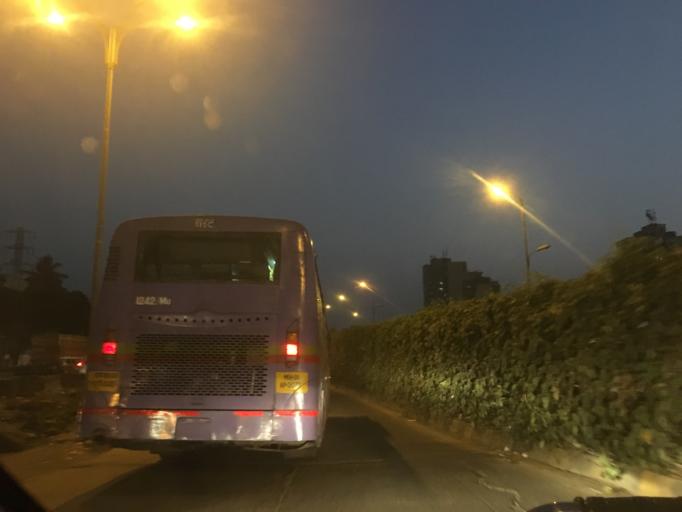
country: IN
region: Maharashtra
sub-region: Thane
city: Airoli
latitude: 19.1495
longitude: 73.0006
